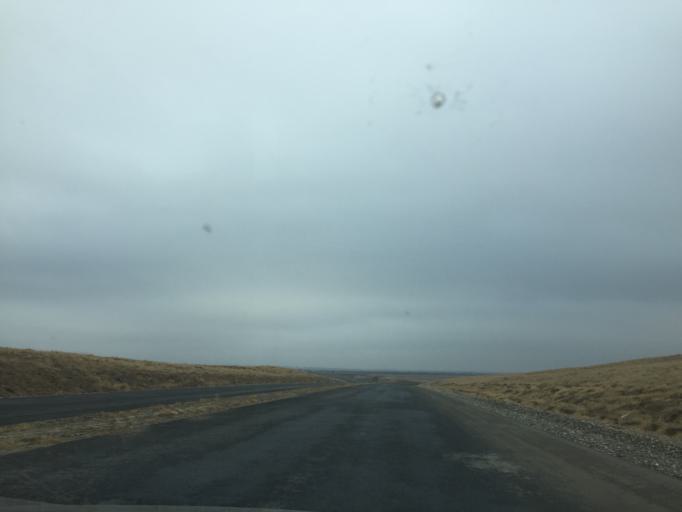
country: KZ
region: Ongtustik Qazaqstan
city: Kokterek
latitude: 42.5442
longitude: 70.1856
